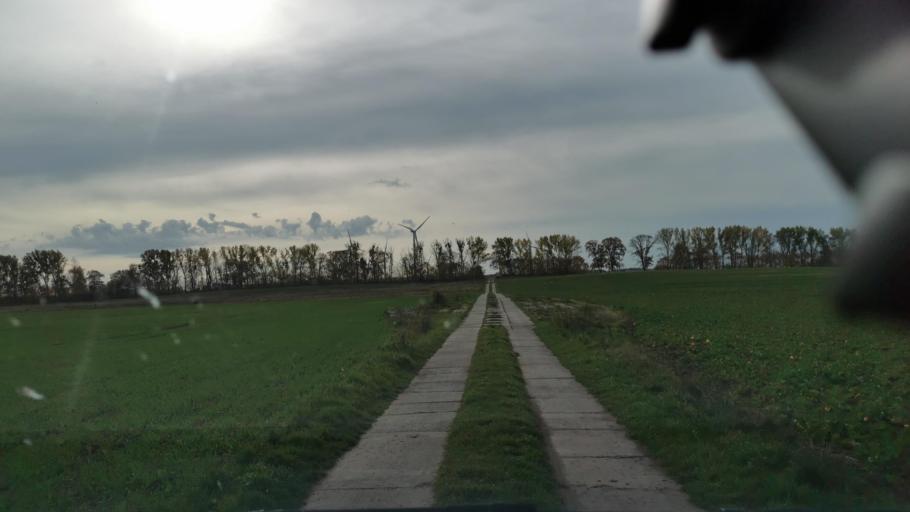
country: DE
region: Brandenburg
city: Eberswalde
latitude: 52.7762
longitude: 13.8554
